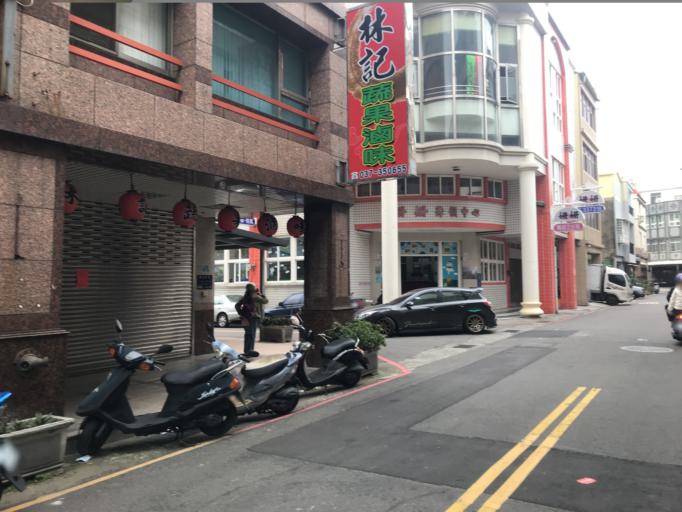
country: TW
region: Taiwan
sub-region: Miaoli
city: Miaoli
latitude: 24.5607
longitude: 120.8190
